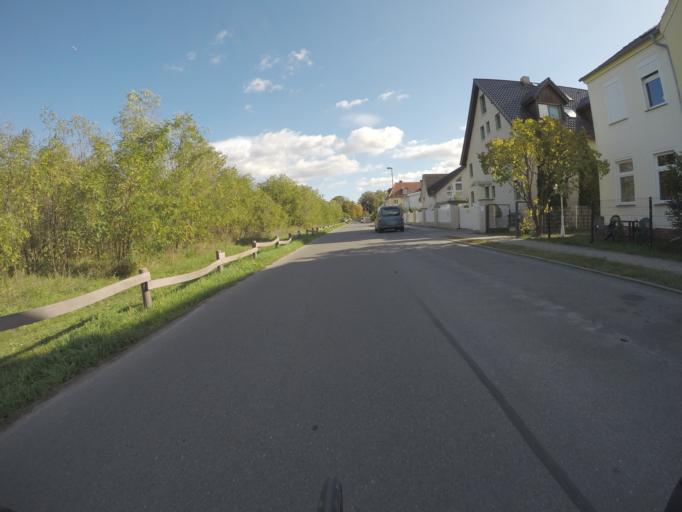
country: DE
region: Berlin
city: Staaken
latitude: 52.5299
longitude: 13.1349
